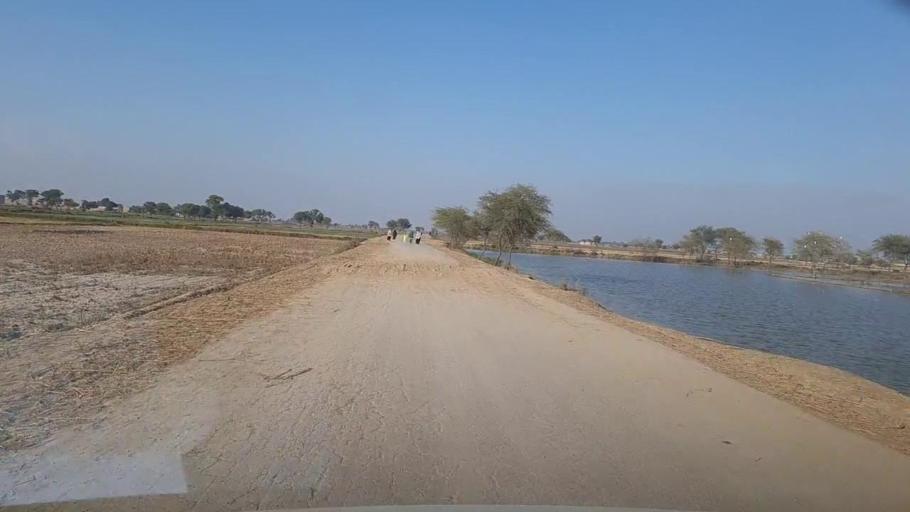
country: PK
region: Sindh
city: Phulji
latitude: 26.8618
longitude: 67.7947
